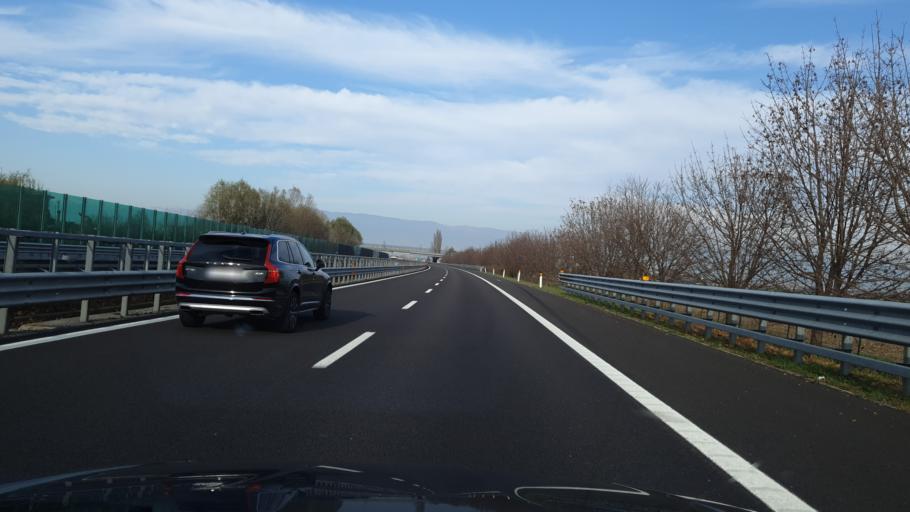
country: IT
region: Veneto
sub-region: Provincia di Vicenza
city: Vigardolo
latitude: 45.6141
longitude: 11.5998
